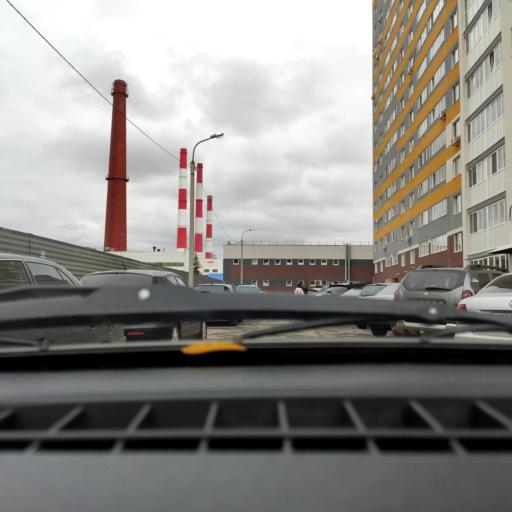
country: RU
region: Bashkortostan
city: Ufa
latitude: 54.7836
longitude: 56.1209
